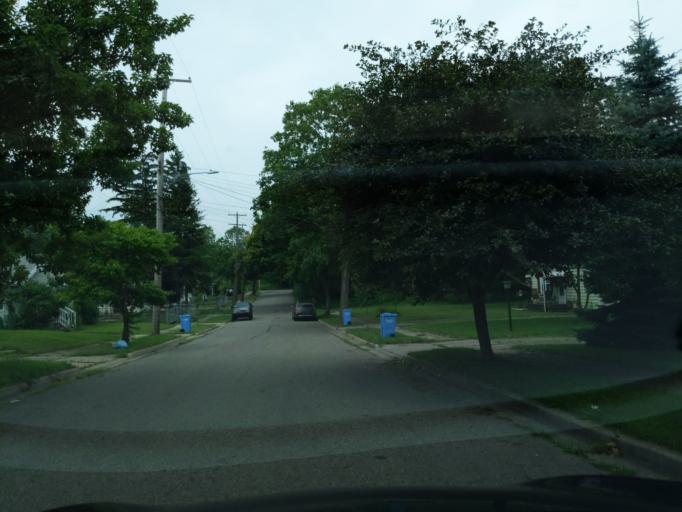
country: US
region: Michigan
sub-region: Ingham County
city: Lansing
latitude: 42.7622
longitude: -84.5394
